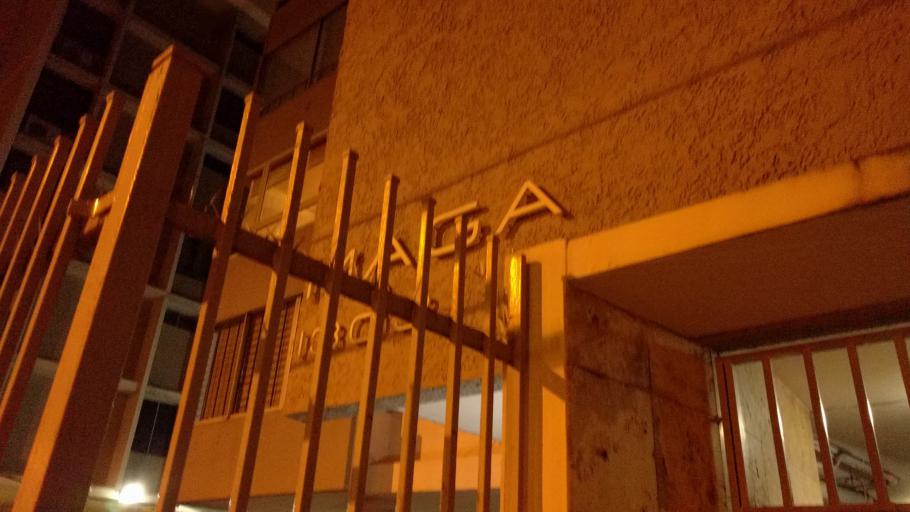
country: PR
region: San Juan
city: San Juan
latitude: 18.4543
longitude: -66.0702
